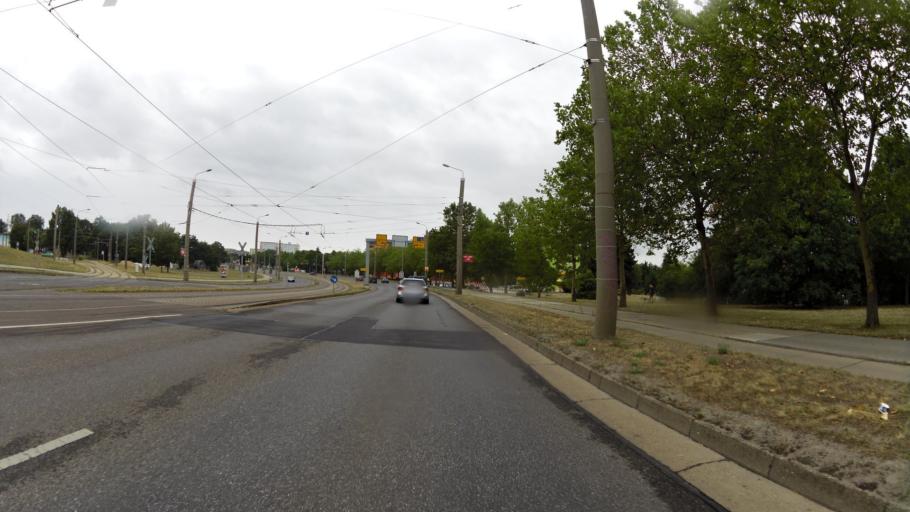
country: DE
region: Brandenburg
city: Cottbus
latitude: 51.7393
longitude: 14.3237
